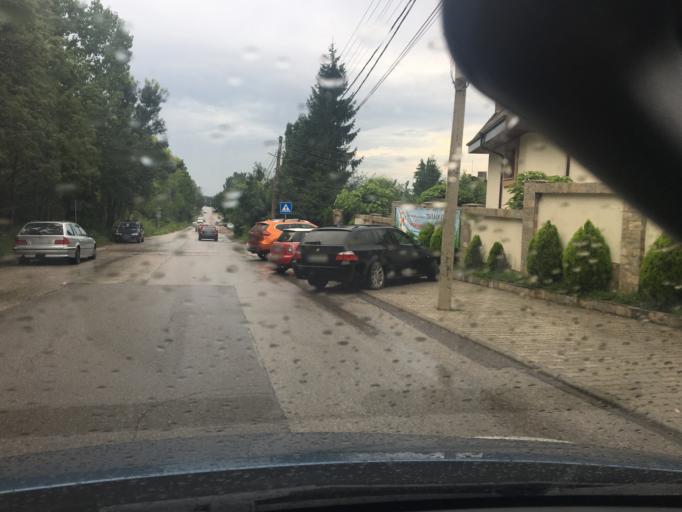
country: BG
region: Sofia-Capital
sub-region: Stolichna Obshtina
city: Sofia
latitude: 42.6380
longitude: 23.2972
